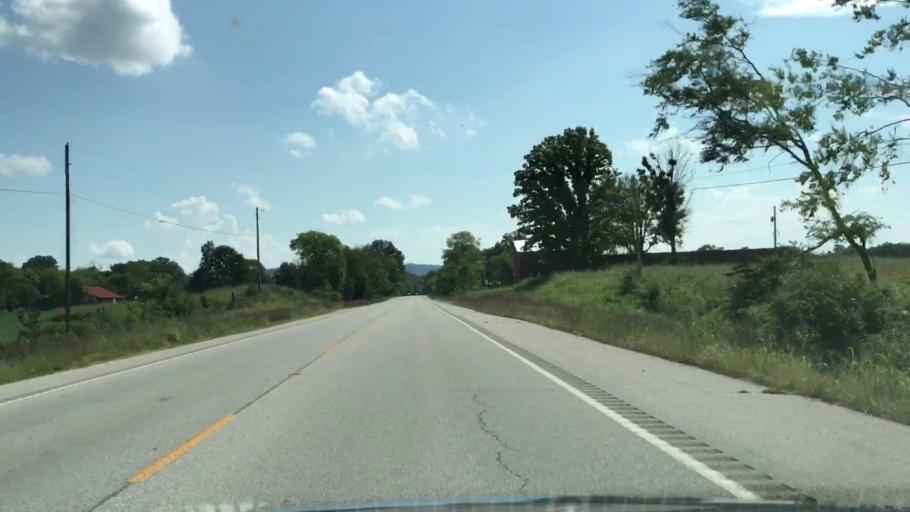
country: US
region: Tennessee
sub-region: Trousdale County
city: Hartsville
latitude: 36.3628
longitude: -86.0638
